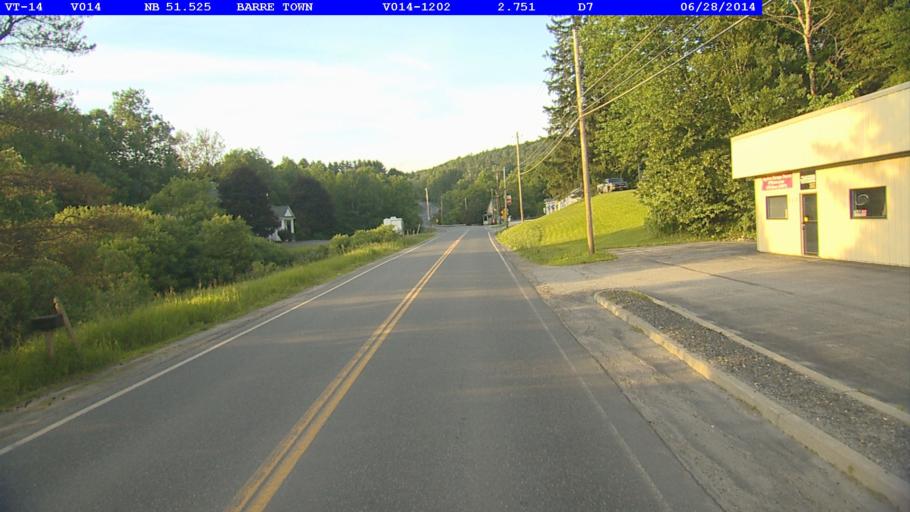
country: US
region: Vermont
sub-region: Washington County
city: Barre
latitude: 44.2185
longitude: -72.4926
